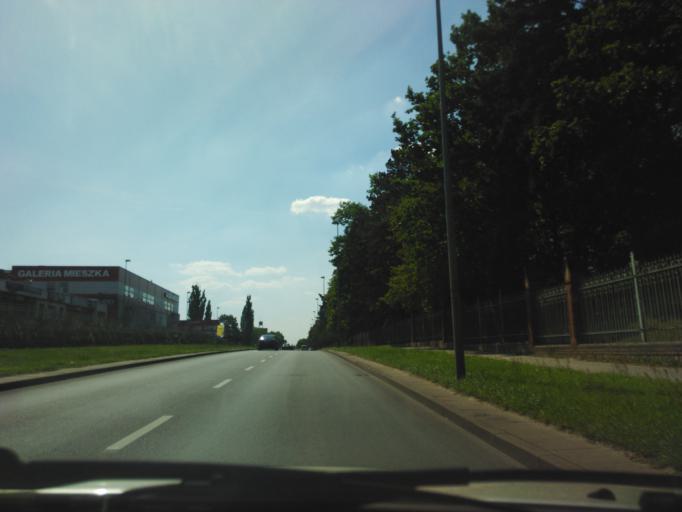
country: PL
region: West Pomeranian Voivodeship
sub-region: Szczecin
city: Szczecin
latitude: 53.4142
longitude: 14.5262
